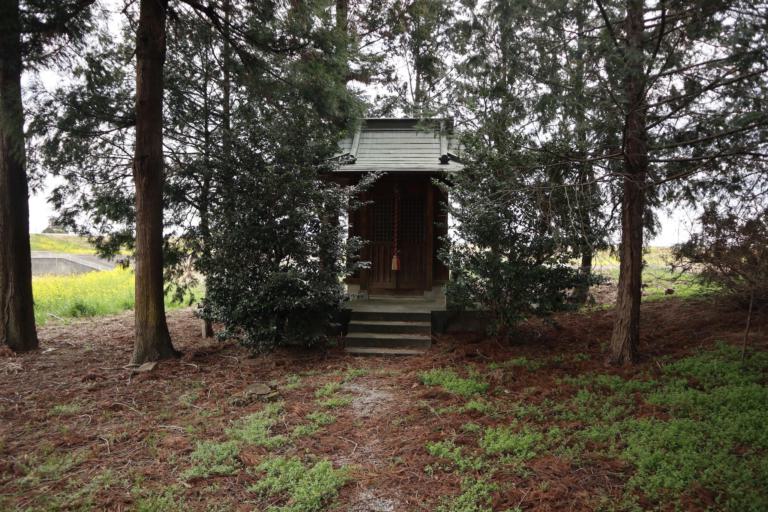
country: JP
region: Gunma
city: Tatebayashi
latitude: 36.2795
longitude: 139.5357
